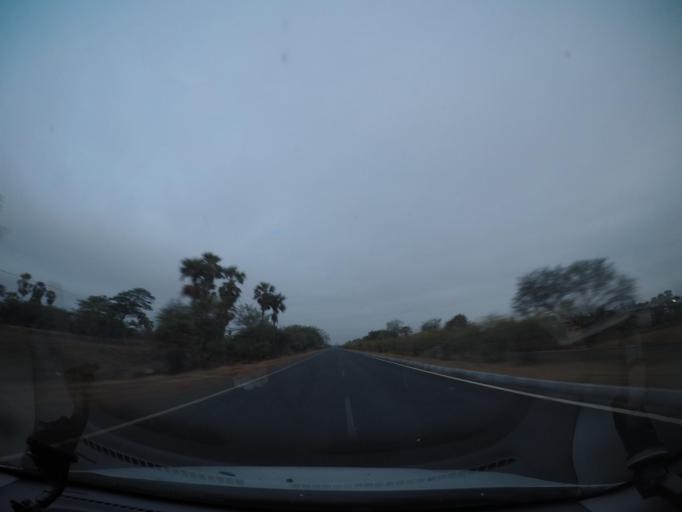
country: IN
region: Andhra Pradesh
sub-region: West Godavari
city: Tadepallegudem
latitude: 16.8102
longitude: 81.3401
